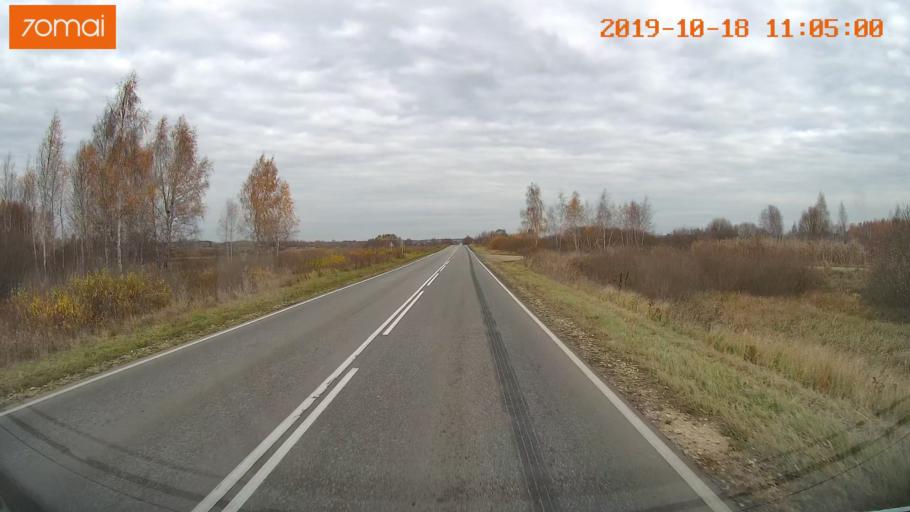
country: RU
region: Tula
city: Kimovsk
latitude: 53.9003
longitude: 38.5415
